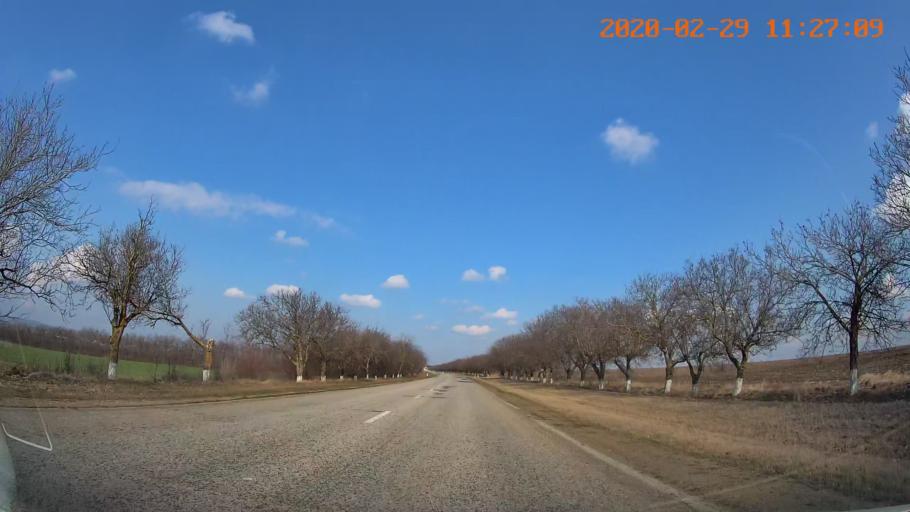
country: MD
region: Telenesti
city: Cocieri
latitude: 47.4638
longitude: 29.1436
